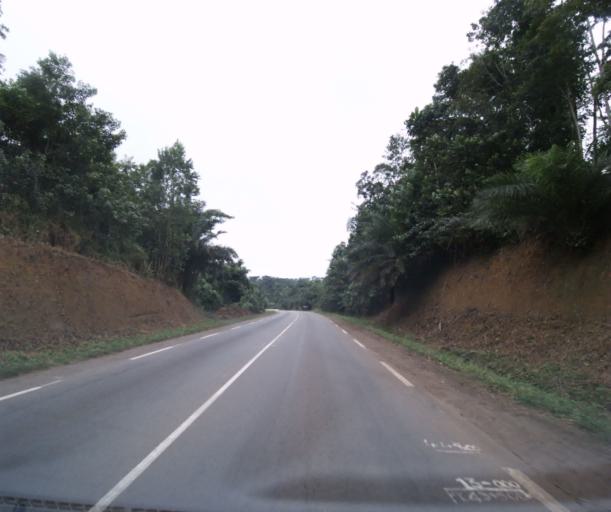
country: CM
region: Centre
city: Mbankomo
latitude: 3.7733
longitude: 11.1656
